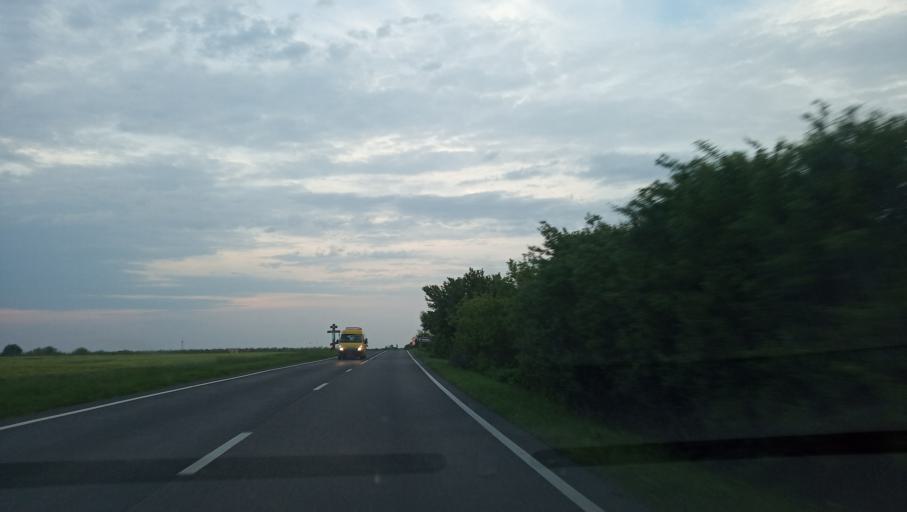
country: RO
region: Timis
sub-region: Comuna Voiteg
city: Voiteg
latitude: 45.4817
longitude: 21.2331
